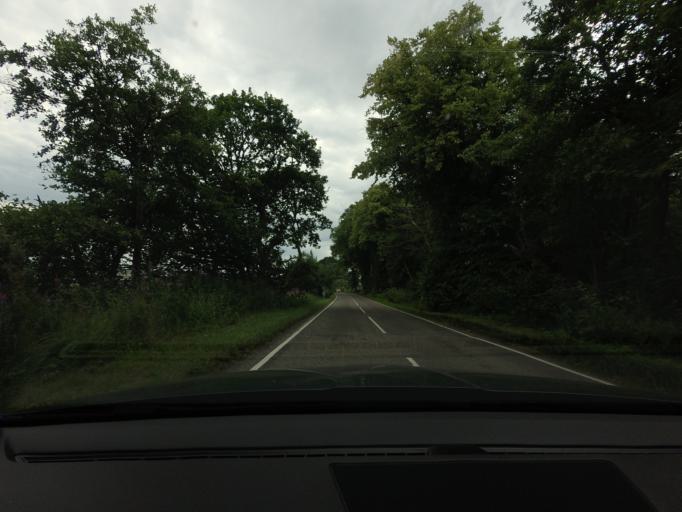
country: GB
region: Scotland
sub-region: Highland
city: Alness
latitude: 57.6932
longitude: -4.2936
